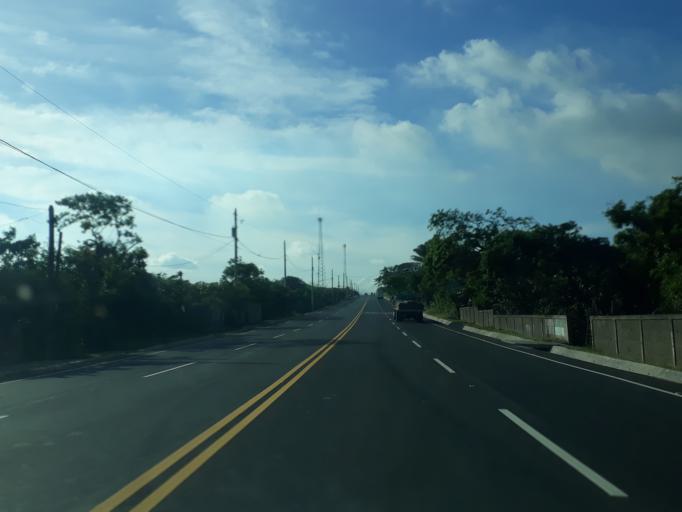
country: NI
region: Managua
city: El Crucero
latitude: 11.9220
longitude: -86.2802
